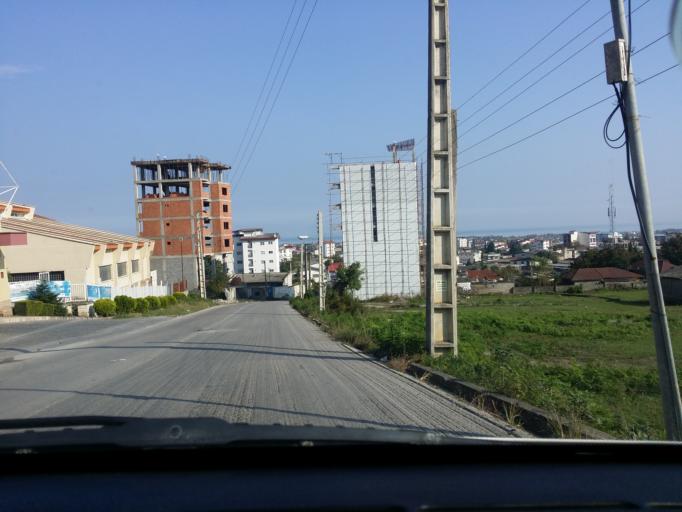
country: IR
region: Mazandaran
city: Chalus
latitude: 36.6452
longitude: 51.4260
